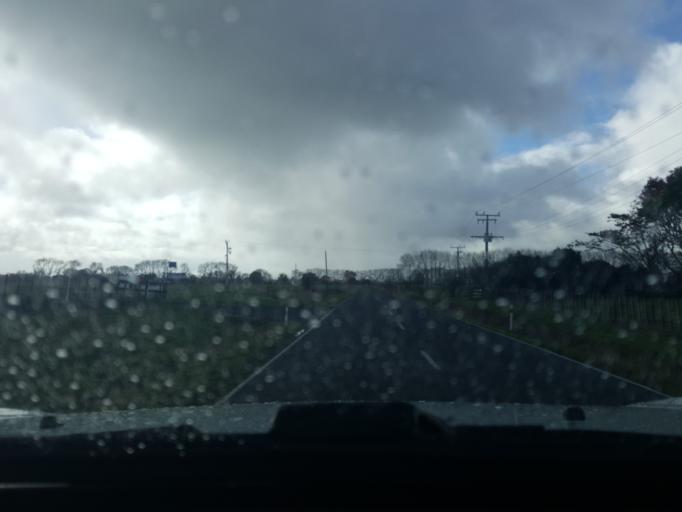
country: NZ
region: Waikato
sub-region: Waikato District
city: Te Kauwhata
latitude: -37.4448
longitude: 175.1179
